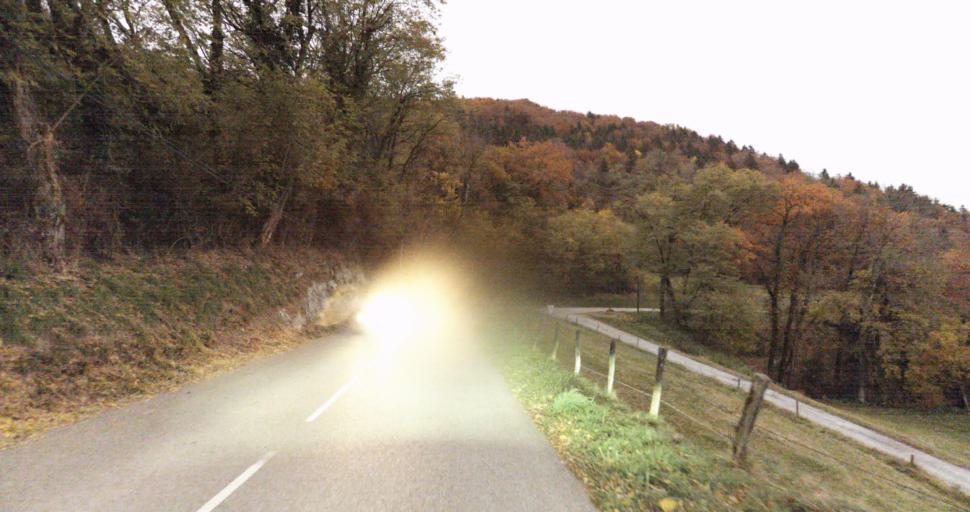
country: FR
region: Rhone-Alpes
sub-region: Departement de la Haute-Savoie
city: Alby-sur-Cheran
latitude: 45.8342
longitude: 6.0126
